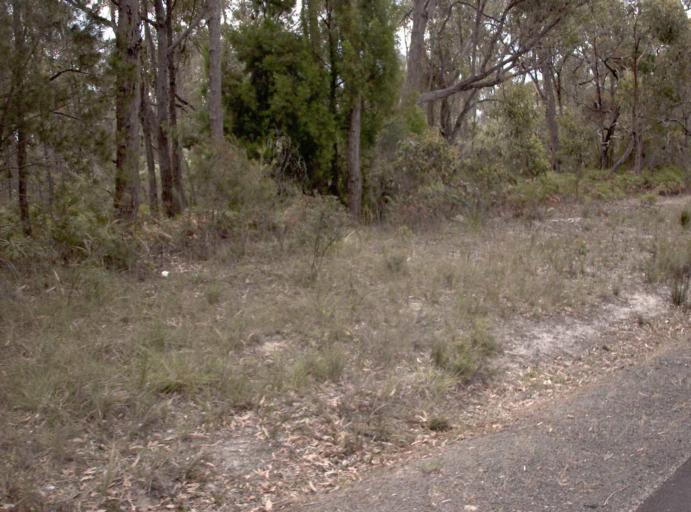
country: AU
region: New South Wales
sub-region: Bega Valley
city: Eden
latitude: -37.4855
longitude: 149.5504
